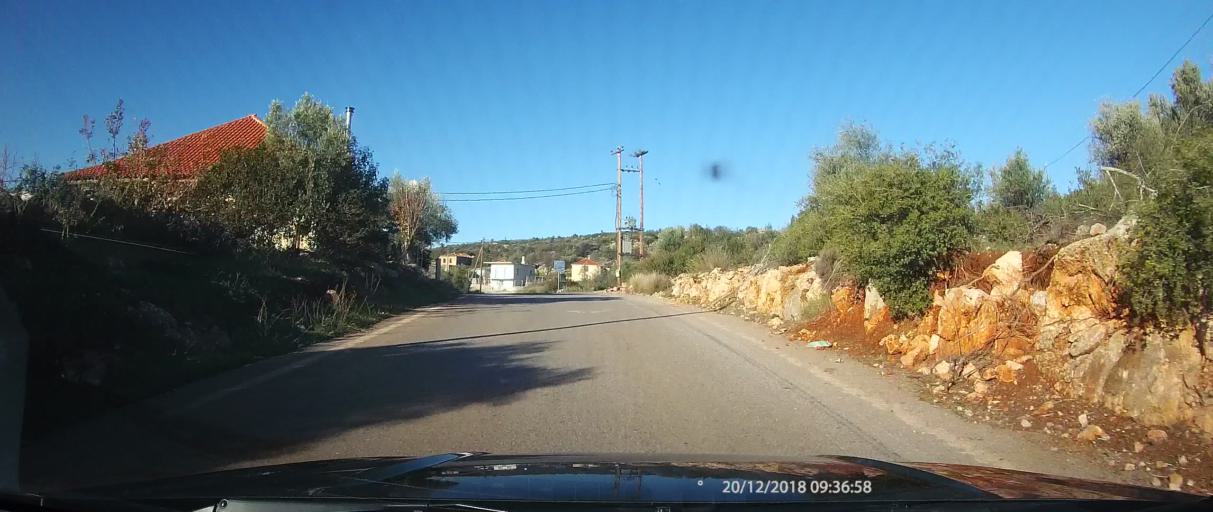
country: GR
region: Peloponnese
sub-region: Nomos Lakonias
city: Kato Glikovrisi
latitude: 36.9385
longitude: 22.8148
